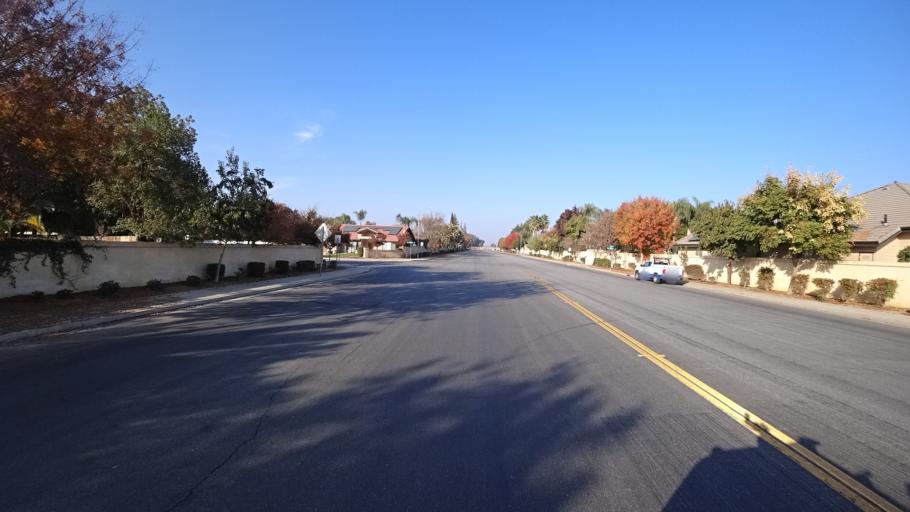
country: US
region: California
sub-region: Kern County
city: Rosedale
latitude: 35.3555
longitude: -119.1544
